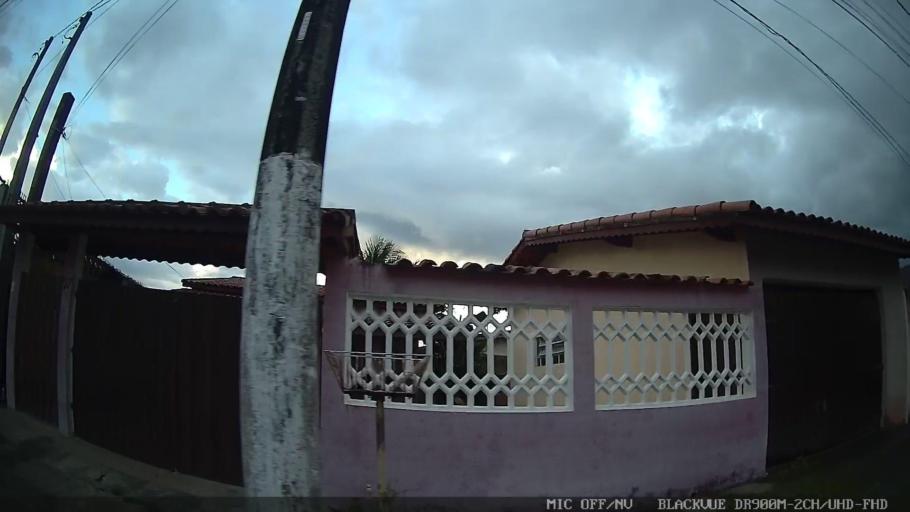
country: BR
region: Sao Paulo
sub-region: Sao Sebastiao
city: Sao Sebastiao
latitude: -23.6918
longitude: -45.4316
